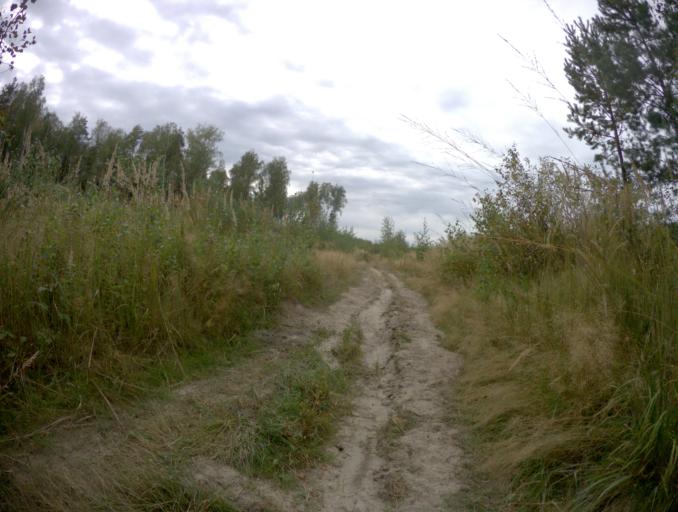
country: RU
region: Vladimir
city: Urshel'skiy
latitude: 55.8151
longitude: 40.2526
